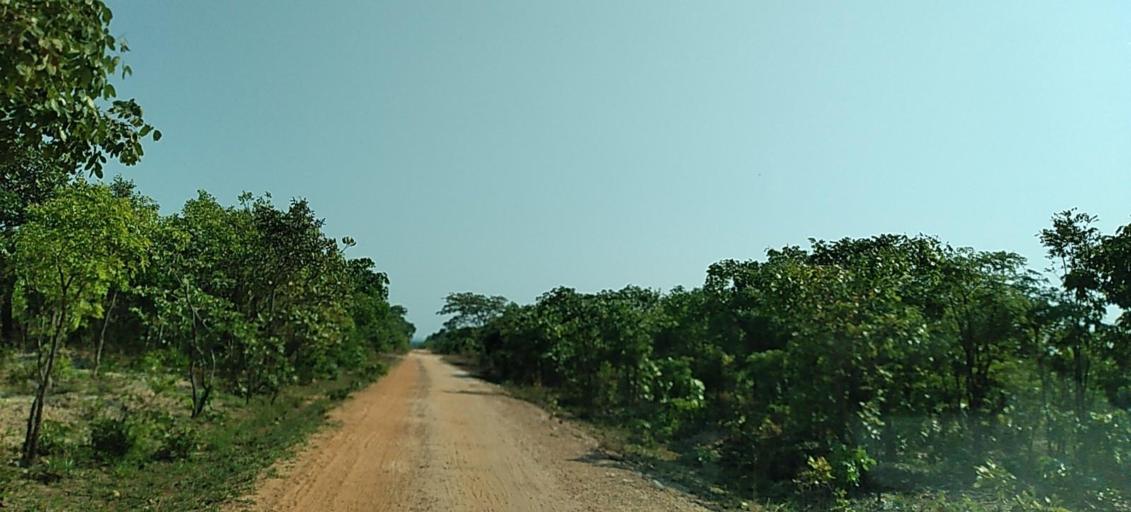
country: ZM
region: Copperbelt
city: Luanshya
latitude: -13.2940
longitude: 28.2505
